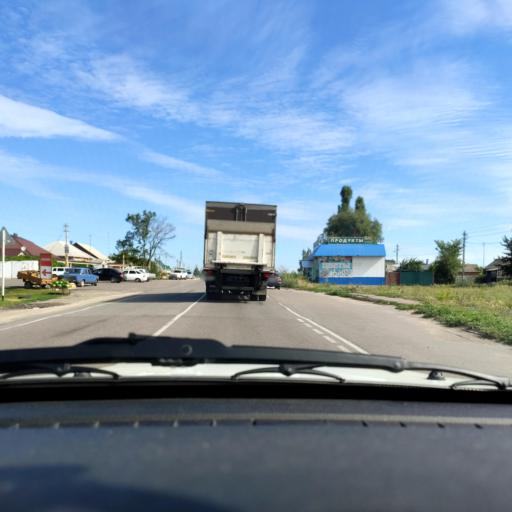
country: RU
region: Voronezj
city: Orlovo
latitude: 51.7534
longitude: 39.5879
